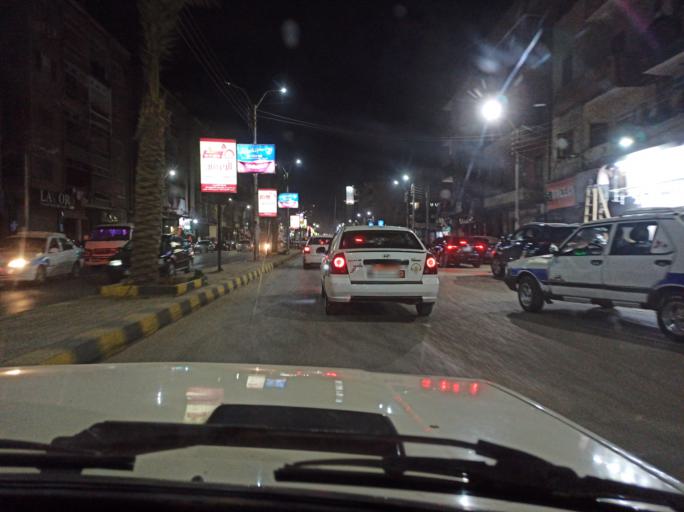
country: EG
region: Muhafazat Bani Suwayf
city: Bani Suwayf
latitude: 29.0710
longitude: 31.1016
